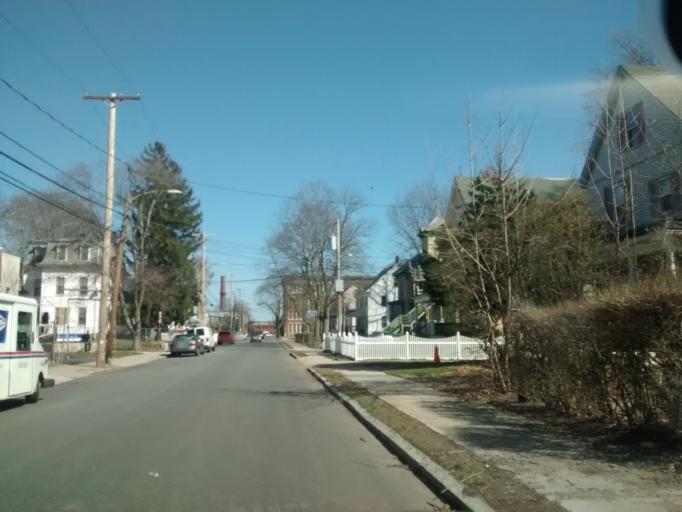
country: US
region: Massachusetts
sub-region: Middlesex County
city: Framingham
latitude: 42.2808
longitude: -71.4138
